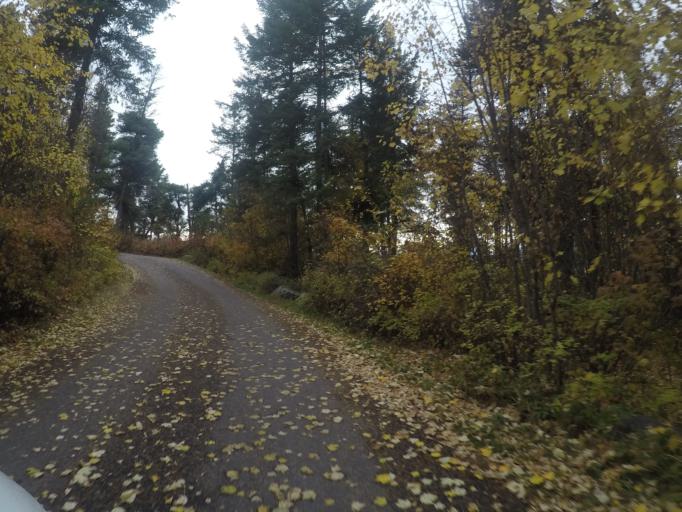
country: US
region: Montana
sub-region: Flathead County
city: Bigfork
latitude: 48.0533
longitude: -114.0824
